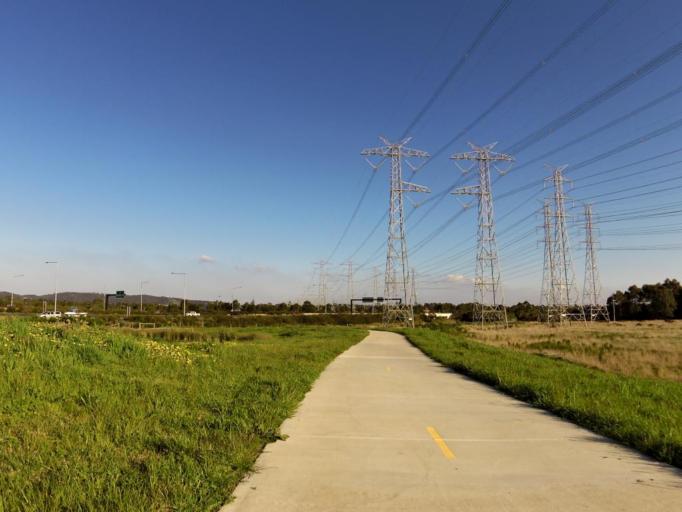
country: AU
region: Victoria
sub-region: Monash
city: Mulgrave
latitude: -37.9151
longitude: 145.2143
